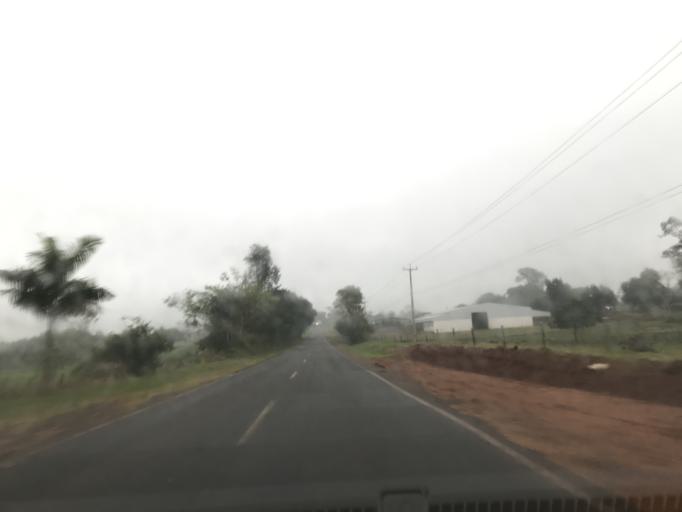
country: PY
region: Canindeyu
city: Salto del Guaira
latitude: -24.1409
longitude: -54.1081
